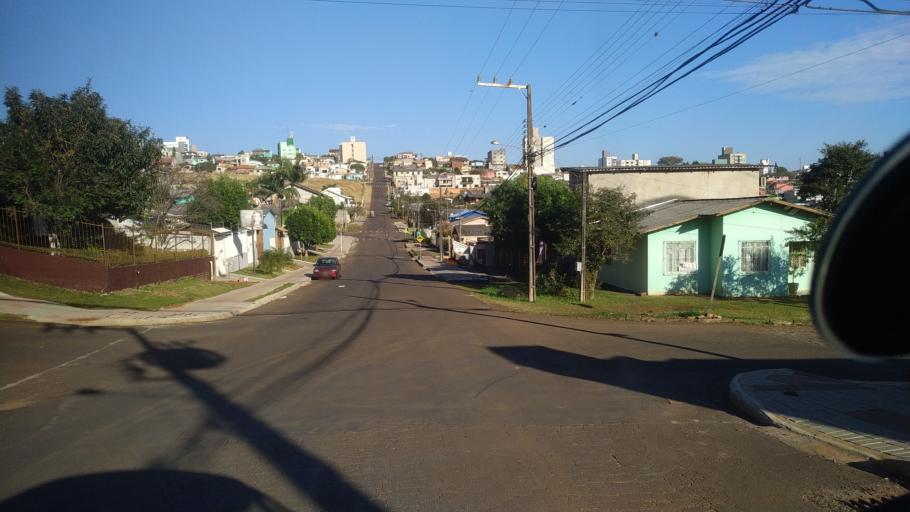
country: BR
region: Santa Catarina
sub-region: Chapeco
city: Chapeco
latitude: -27.1177
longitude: -52.5991
